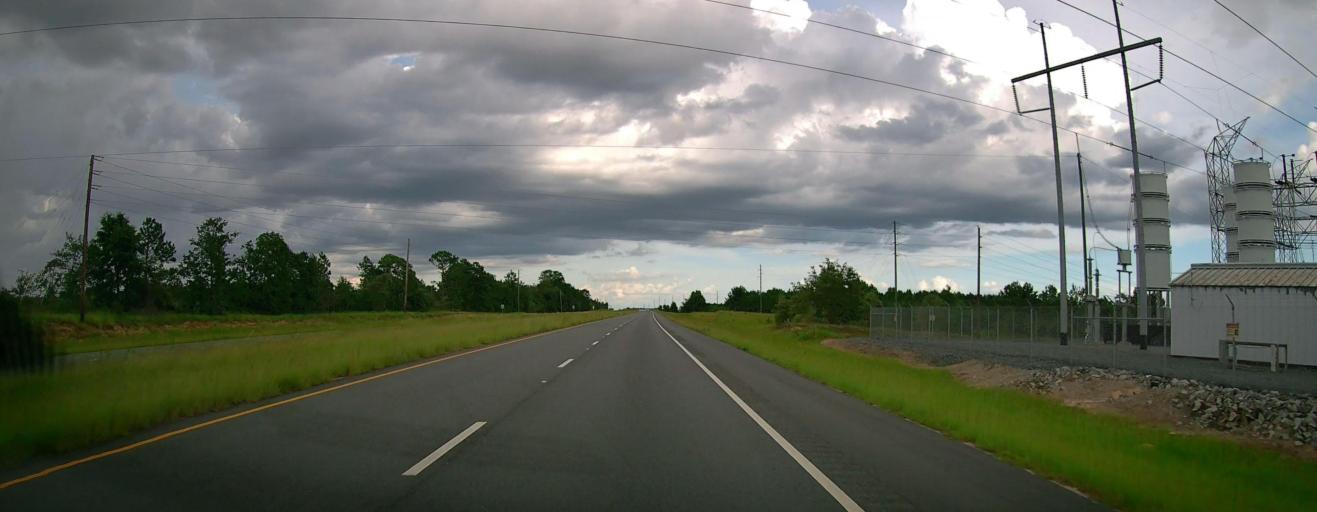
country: US
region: Georgia
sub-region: Taylor County
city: Butler
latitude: 32.5719
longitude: -84.2901
